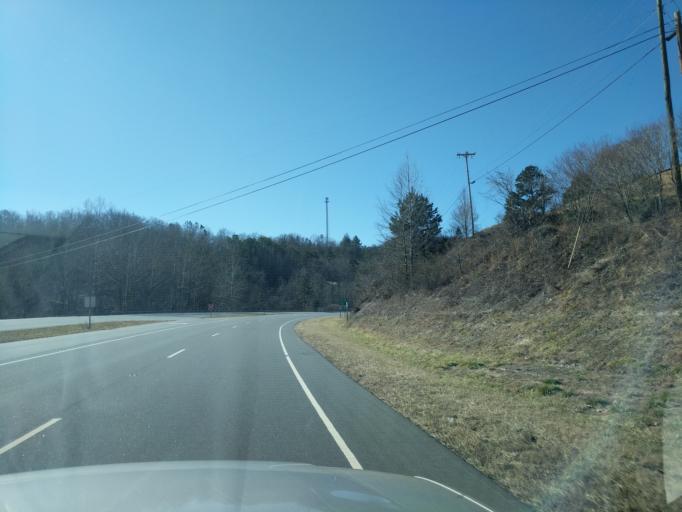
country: US
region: North Carolina
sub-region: Swain County
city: Bryson City
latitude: 35.3735
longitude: -83.5029
